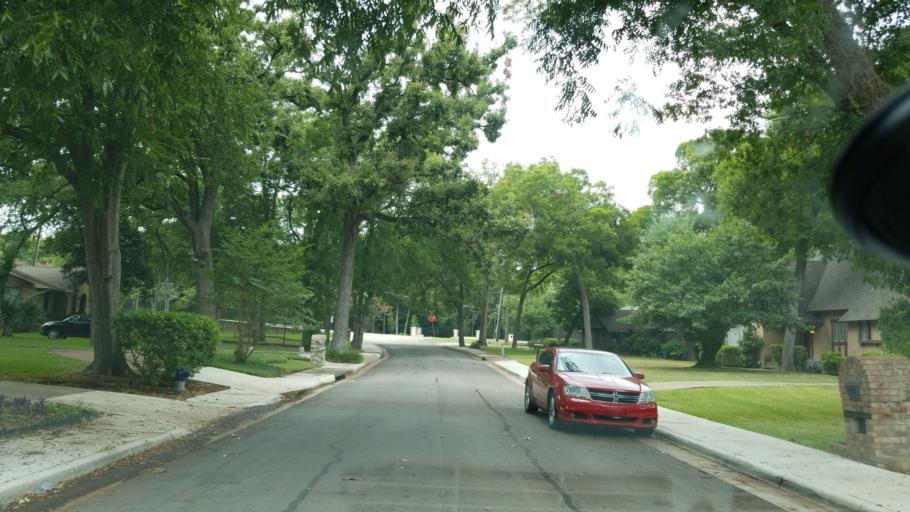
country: US
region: Texas
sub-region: Dallas County
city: Duncanville
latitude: 32.6631
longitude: -96.8560
